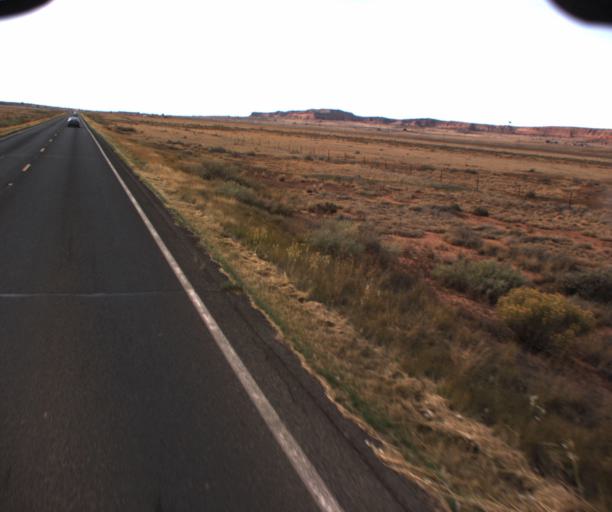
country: US
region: Arizona
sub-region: Apache County
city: Ganado
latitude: 35.7867
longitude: -109.6177
